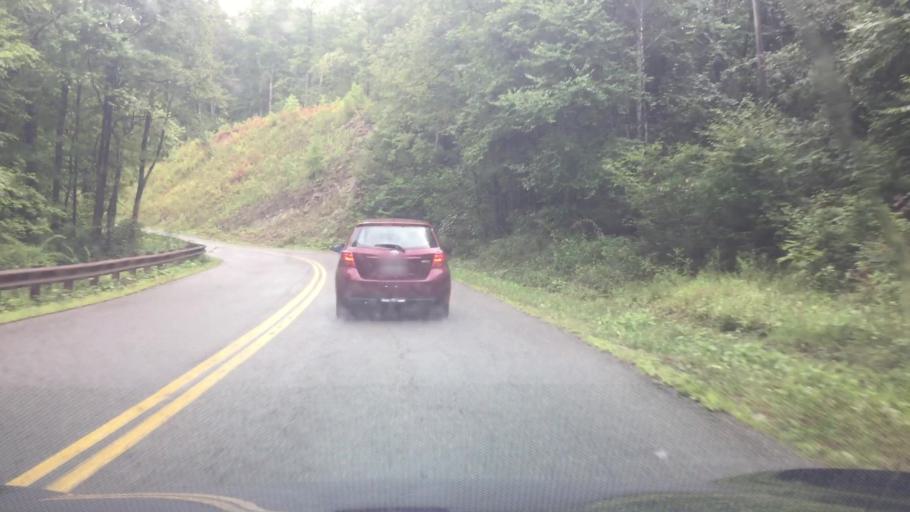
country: US
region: Virginia
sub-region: Smyth County
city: Atkins
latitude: 36.8255
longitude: -81.4150
